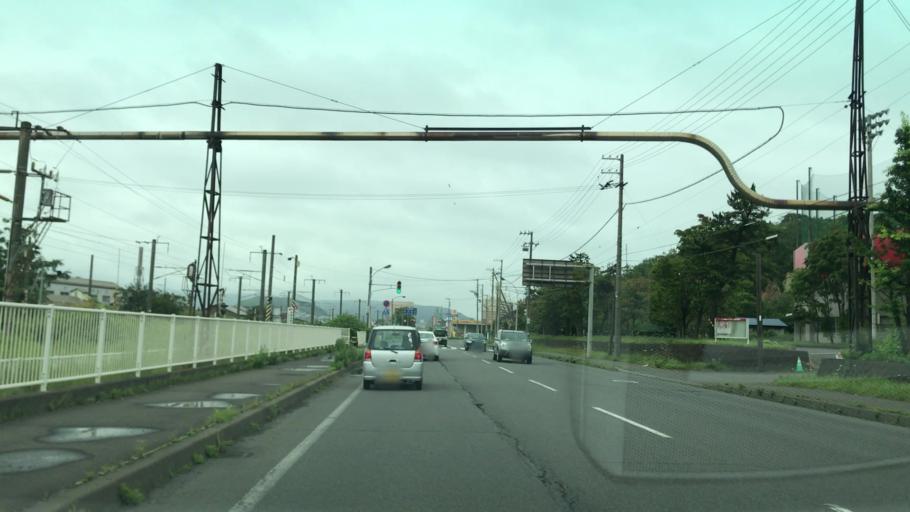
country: JP
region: Hokkaido
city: Muroran
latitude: 42.3391
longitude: 141.0154
